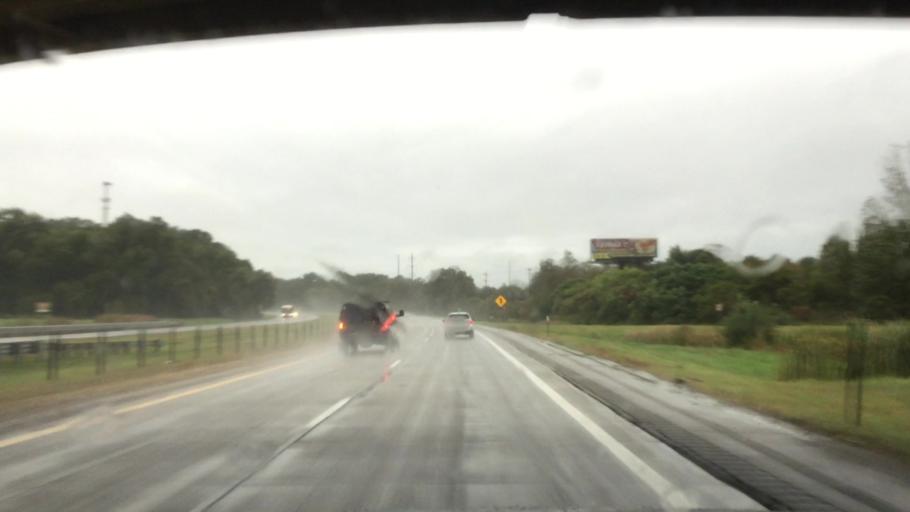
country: US
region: Michigan
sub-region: Berrien County
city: Coloma
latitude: 42.1760
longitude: -86.3055
